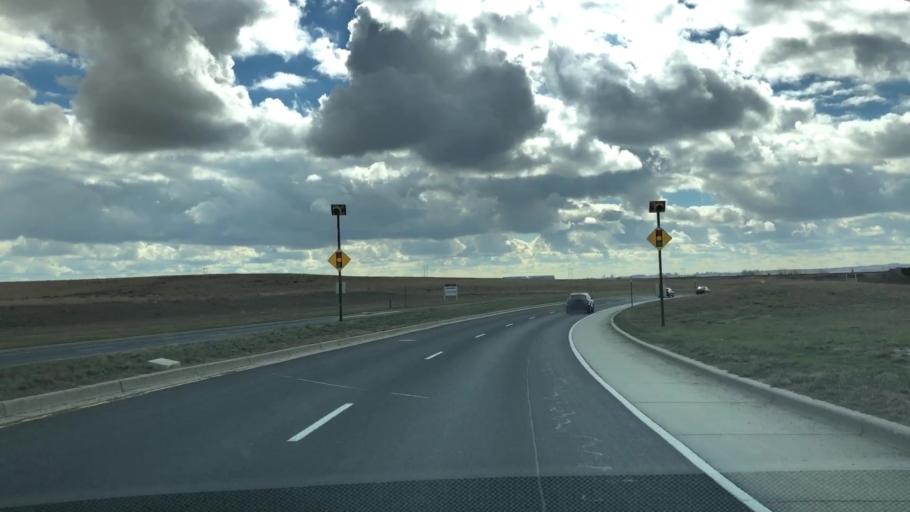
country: US
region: Colorado
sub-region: Larimer County
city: Loveland
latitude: 40.4196
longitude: -104.9836
